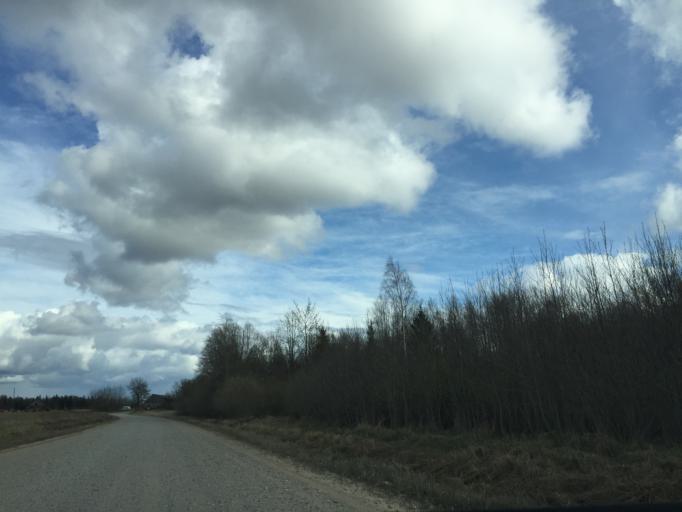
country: LV
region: Limbazu Rajons
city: Limbazi
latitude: 57.6086
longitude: 24.7879
